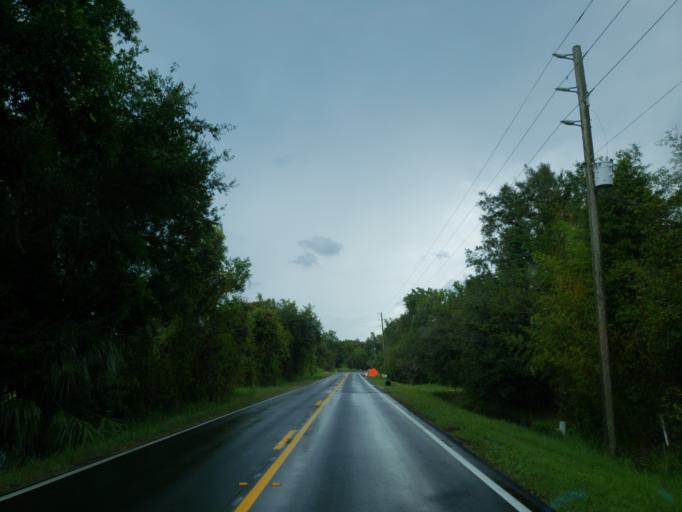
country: US
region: Florida
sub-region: Pasco County
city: Land O' Lakes
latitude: 28.2985
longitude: -82.4317
